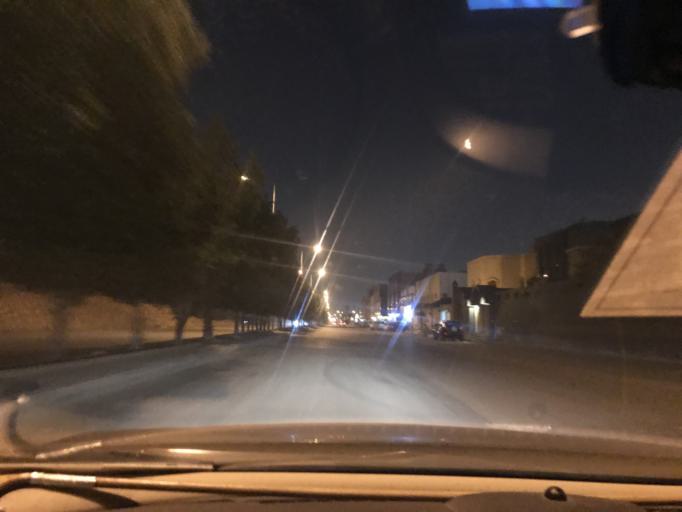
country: SA
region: Ar Riyad
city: Riyadh
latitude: 24.7573
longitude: 46.7554
